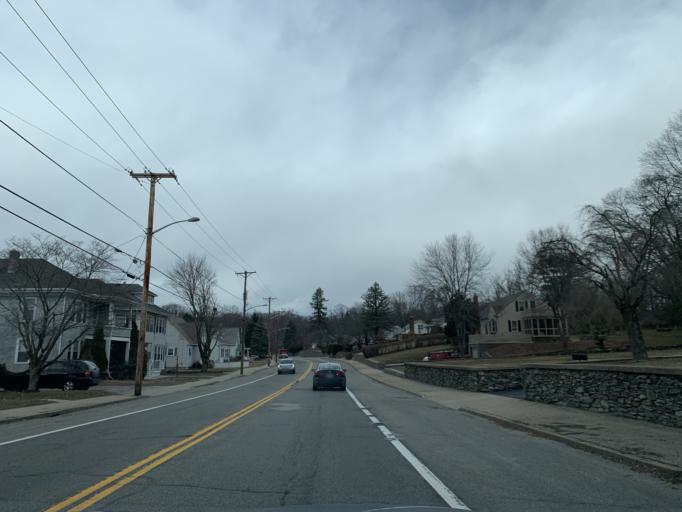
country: US
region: Rhode Island
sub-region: Providence County
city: Cumberland Hill
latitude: 42.0089
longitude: -71.4774
